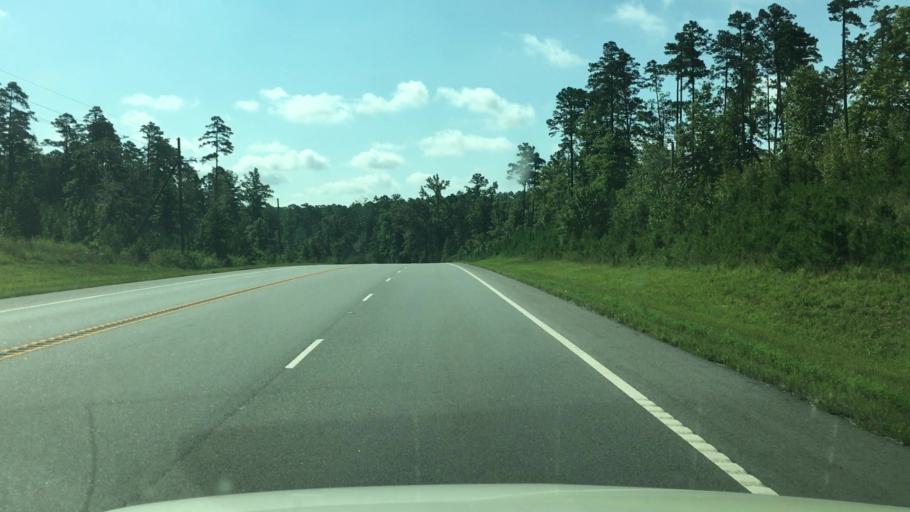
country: US
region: Arkansas
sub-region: Garland County
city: Rockwell
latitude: 34.5203
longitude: -93.3159
